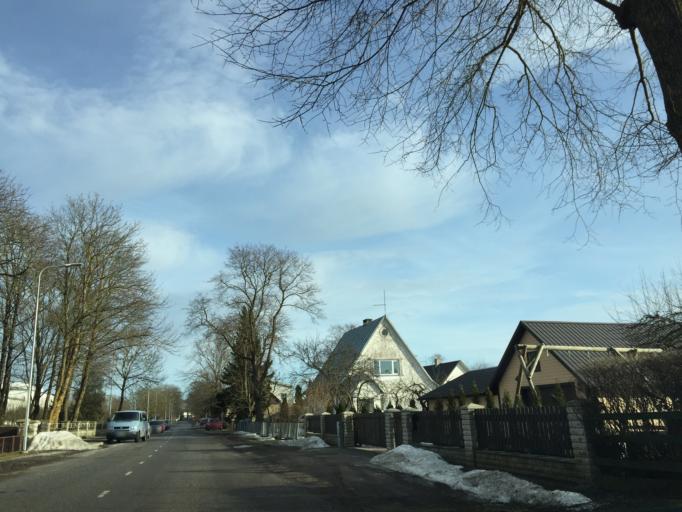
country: EE
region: Saare
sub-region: Kuressaare linn
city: Kuressaare
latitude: 58.2495
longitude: 22.4713
